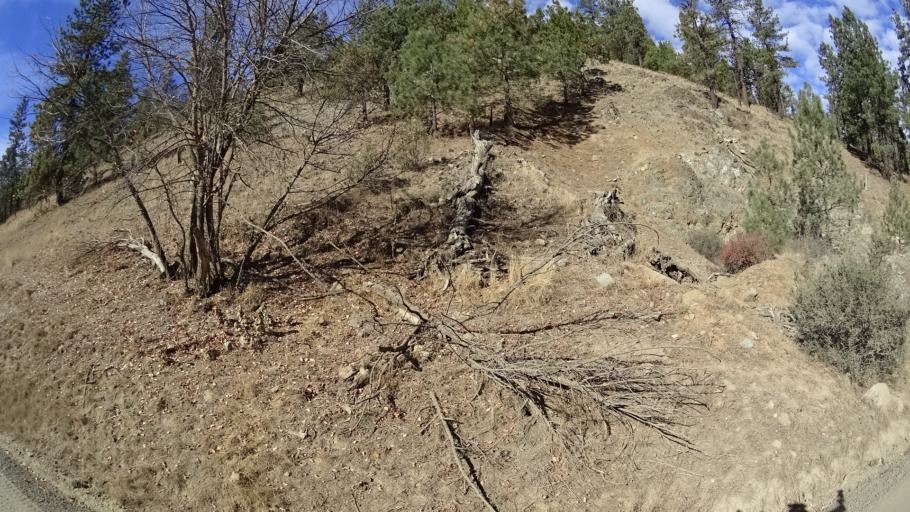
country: US
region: California
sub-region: Siskiyou County
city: Yreka
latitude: 41.6230
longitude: -122.7156
